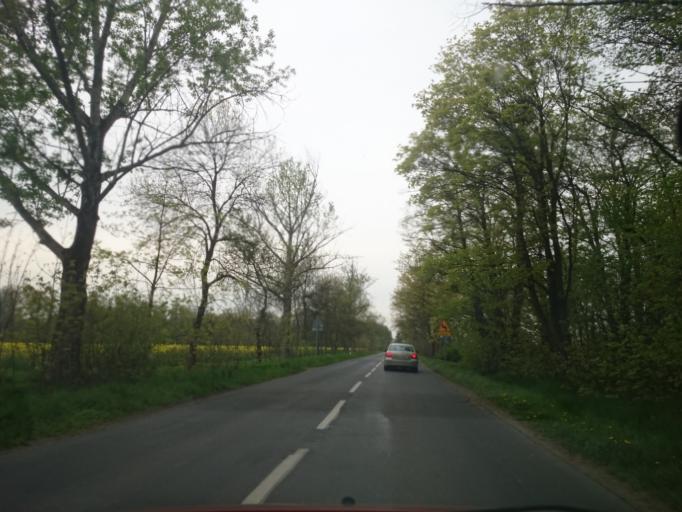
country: PL
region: Opole Voivodeship
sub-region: Powiat brzeski
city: Grodkow
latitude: 50.6494
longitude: 17.4404
